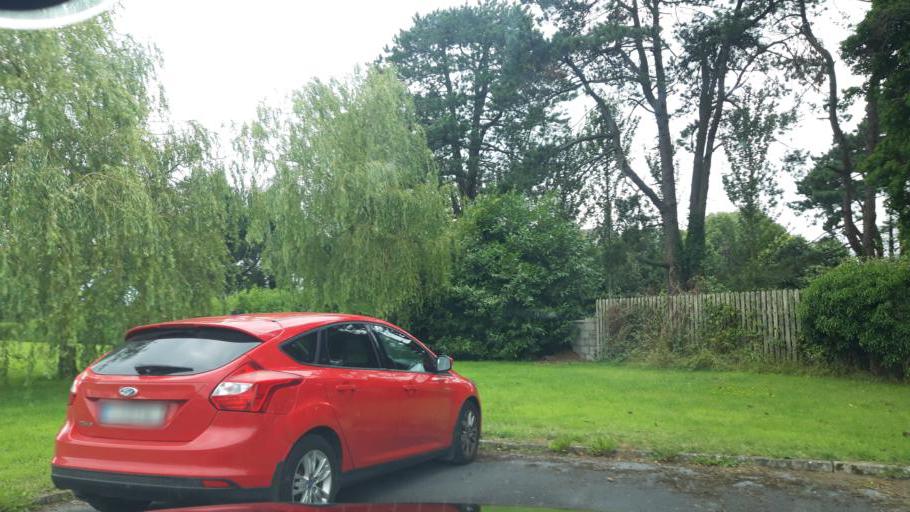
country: IE
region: Leinster
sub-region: Kilkenny
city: Ballyragget
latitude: 52.7889
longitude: -7.3290
